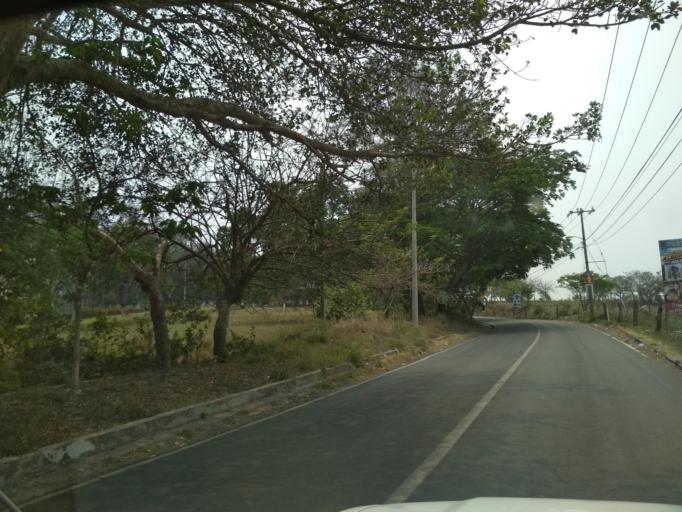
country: MX
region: Veracruz
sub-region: Veracruz
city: Las Amapolas
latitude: 19.1511
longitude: -96.2232
